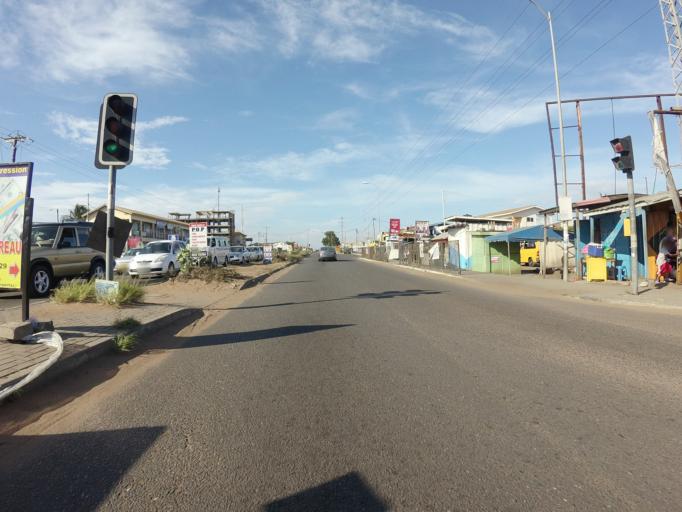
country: GH
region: Greater Accra
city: Nungua
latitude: 5.6242
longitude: -0.0691
